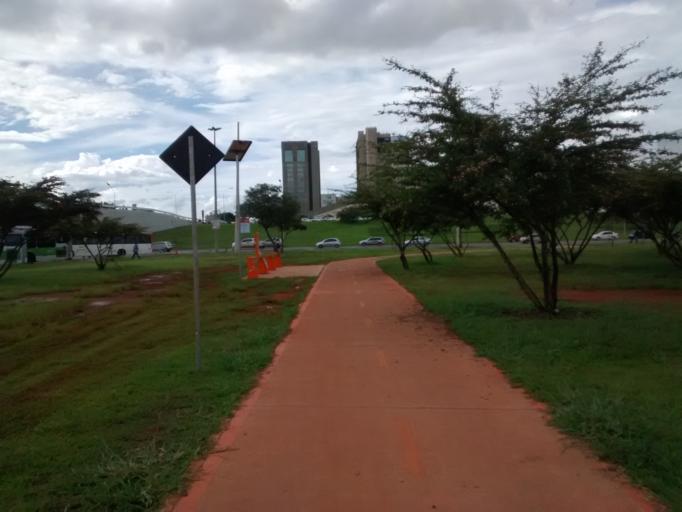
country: BR
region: Federal District
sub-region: Brasilia
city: Brasilia
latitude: -15.7942
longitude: -47.8815
